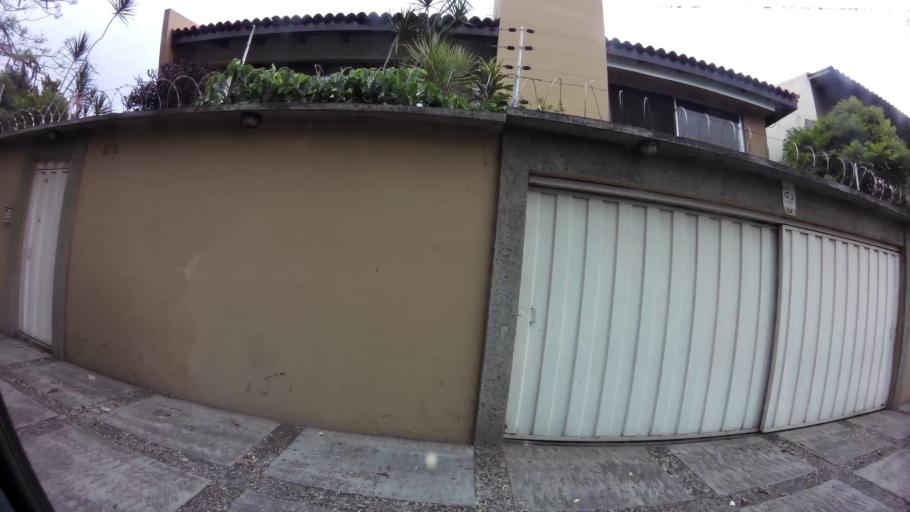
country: HN
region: Francisco Morazan
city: Tegucigalpa
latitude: 14.0933
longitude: -87.1797
